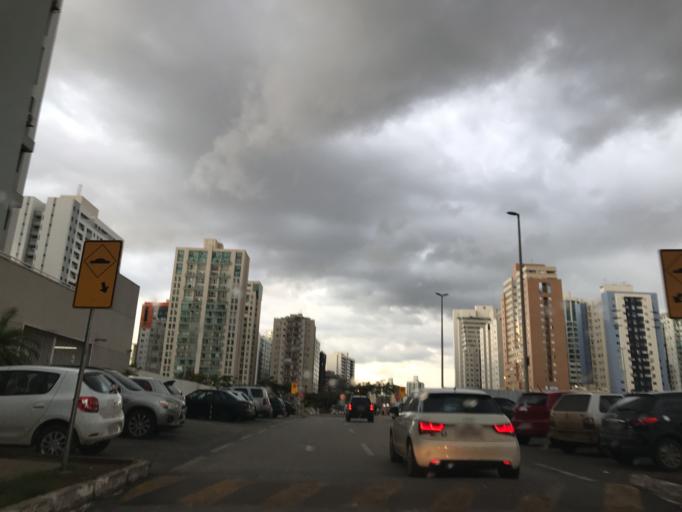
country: BR
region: Federal District
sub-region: Brasilia
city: Brasilia
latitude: -15.8370
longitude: -48.0184
